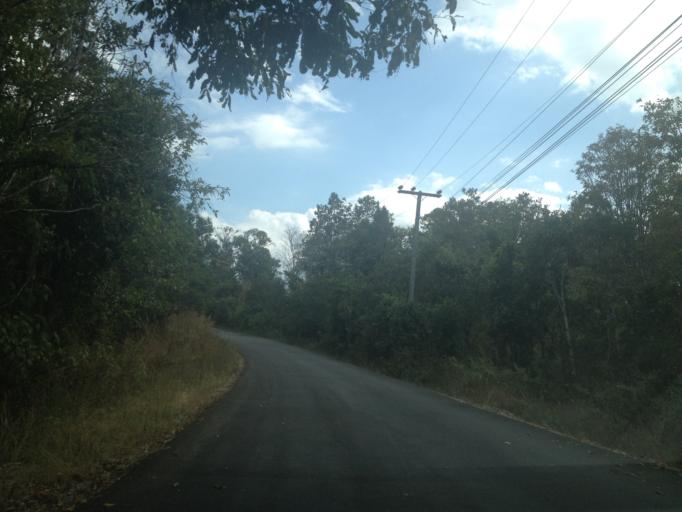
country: TH
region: Mae Hong Son
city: Ban Huai I Huak
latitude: 18.1368
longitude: 98.2192
